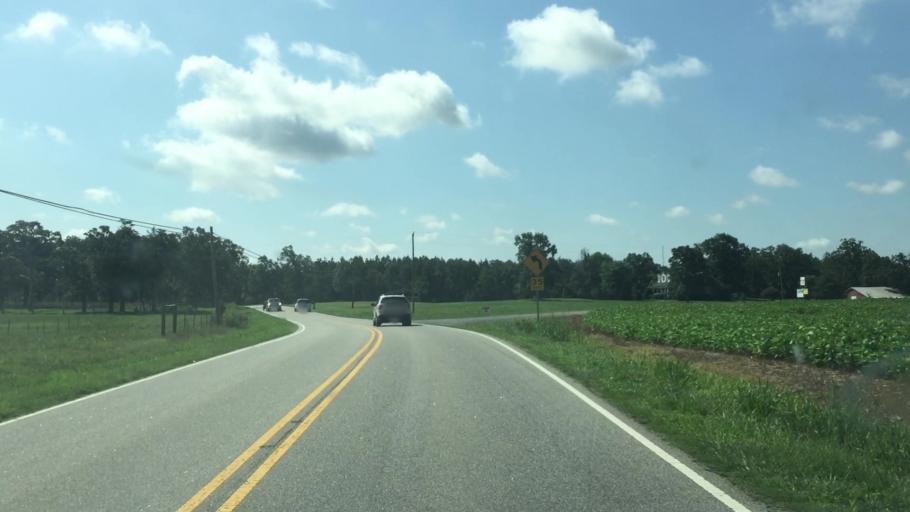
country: US
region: North Carolina
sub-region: Anson County
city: Polkton
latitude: 35.0333
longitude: -80.2439
